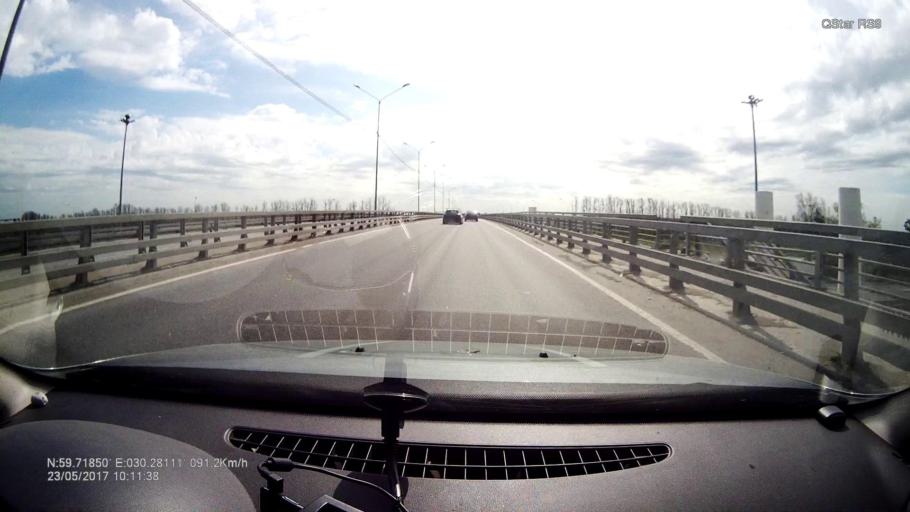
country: RU
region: St.-Petersburg
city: Aleksandrovskaya
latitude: 59.7186
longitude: 30.2811
